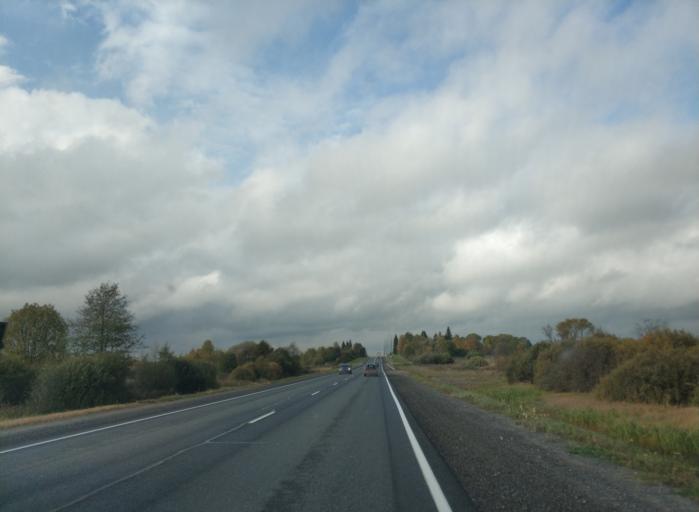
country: RU
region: Pskov
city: Ostrov
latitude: 57.1106
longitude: 28.5353
